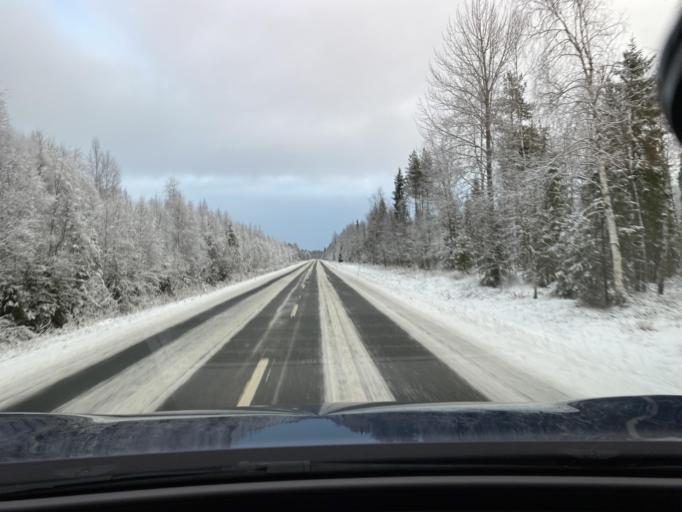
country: FI
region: Lapland
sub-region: Rovaniemi
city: Ranua
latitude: 65.9617
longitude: 26.0409
